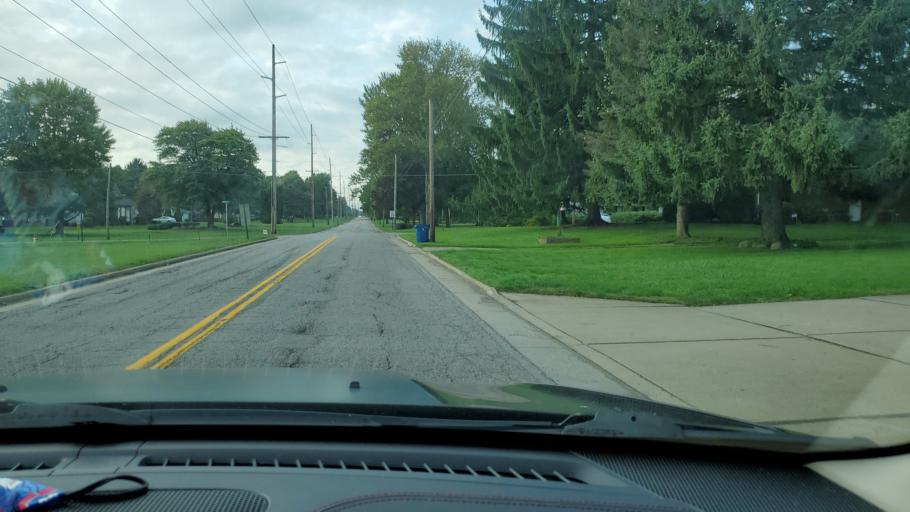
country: US
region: Ohio
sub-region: Mahoning County
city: Struthers
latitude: 41.0472
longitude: -80.6215
